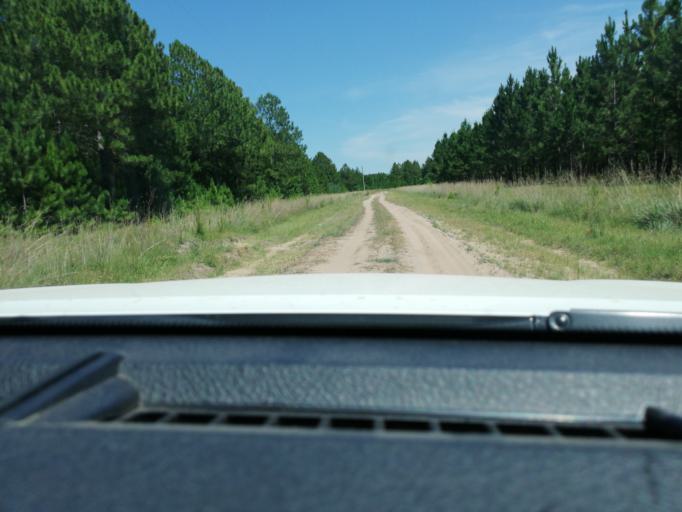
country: AR
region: Corrientes
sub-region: Departamento de San Miguel
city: San Miguel
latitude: -28.0275
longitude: -57.4751
